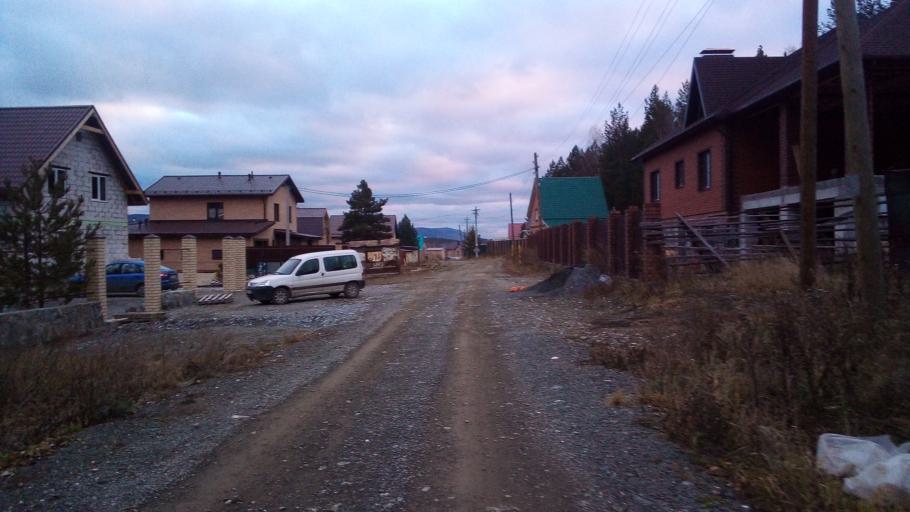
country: RU
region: Chelyabinsk
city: Turgoyak
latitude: 55.1773
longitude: 60.1312
